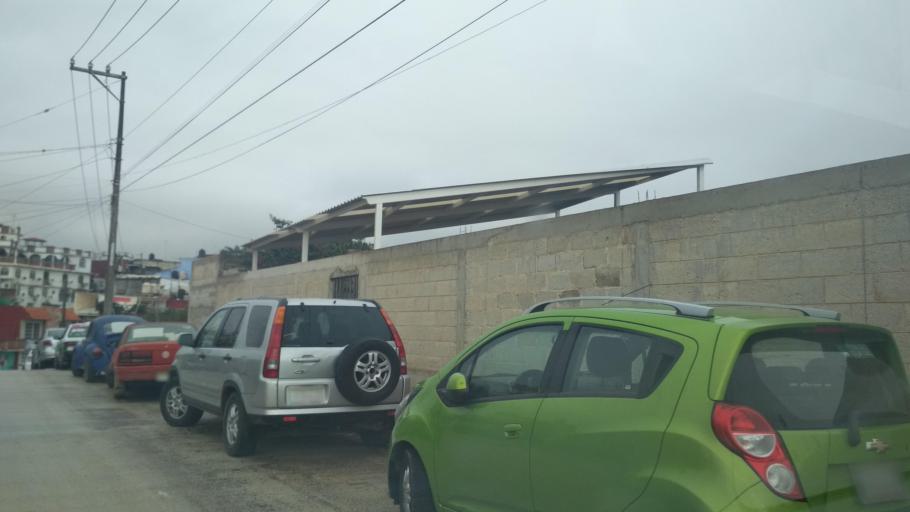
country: MX
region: Veracruz
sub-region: Emiliano Zapata
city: Las Trancas
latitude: 19.5047
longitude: -96.8694
